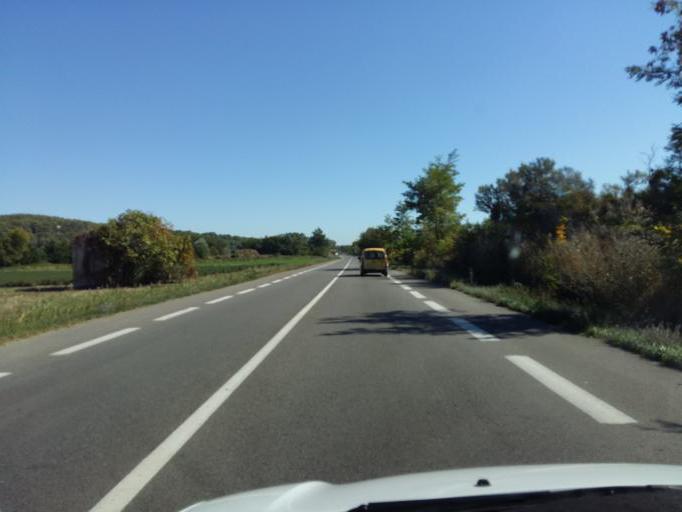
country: FR
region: Provence-Alpes-Cote d'Azur
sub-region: Departement des Bouches-du-Rhone
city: Charleval
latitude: 43.7518
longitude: 5.2608
